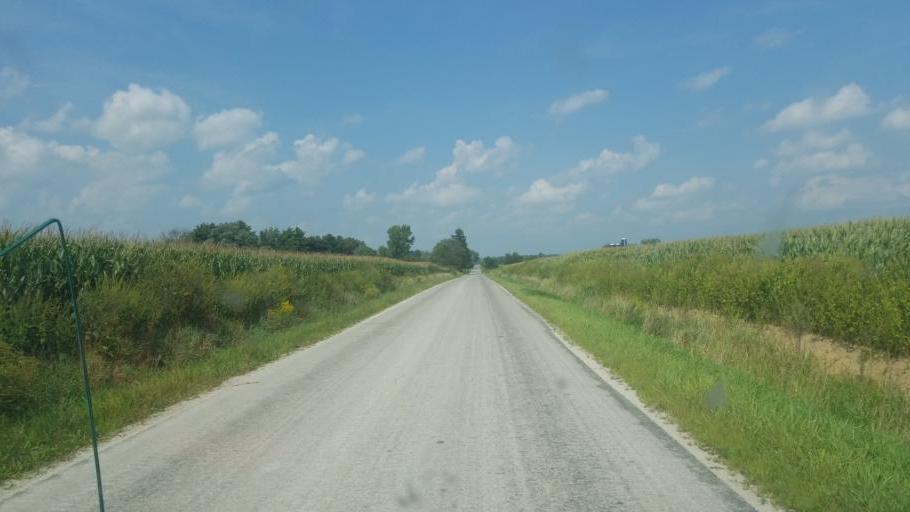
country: US
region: Ohio
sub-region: Huron County
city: Greenwich
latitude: 40.9584
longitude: -82.4316
